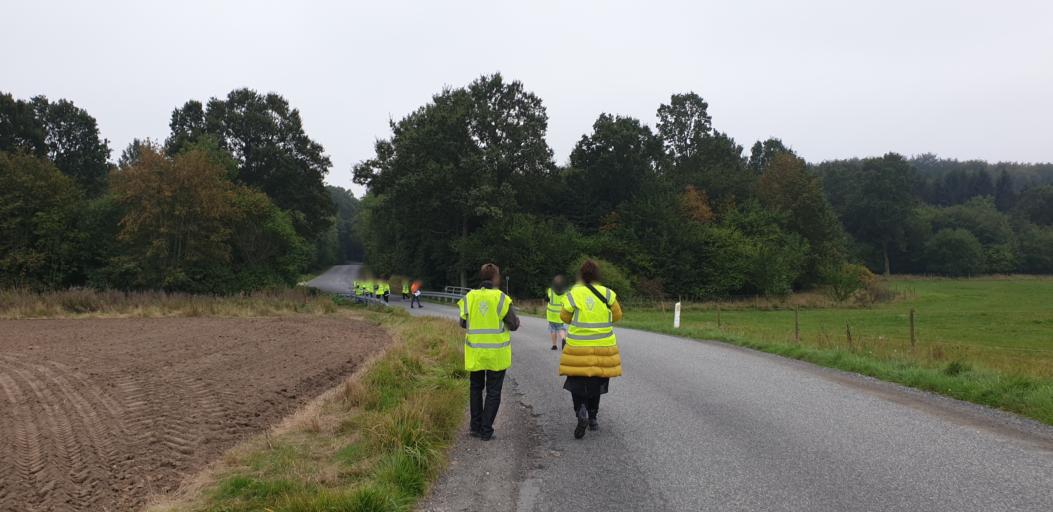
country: DK
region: Zealand
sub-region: Koge Kommune
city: Koge
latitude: 55.3741
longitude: 12.1136
